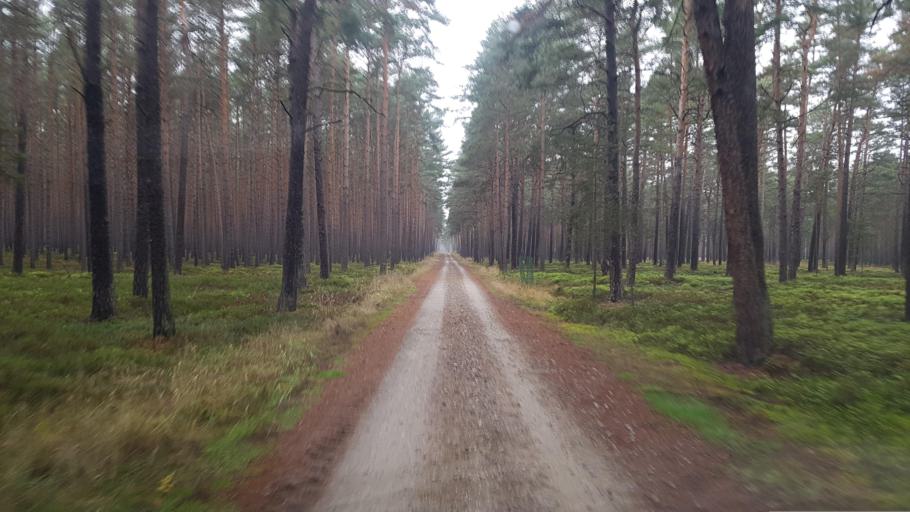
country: DE
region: Brandenburg
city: Sallgast
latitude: 51.6417
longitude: 13.8186
